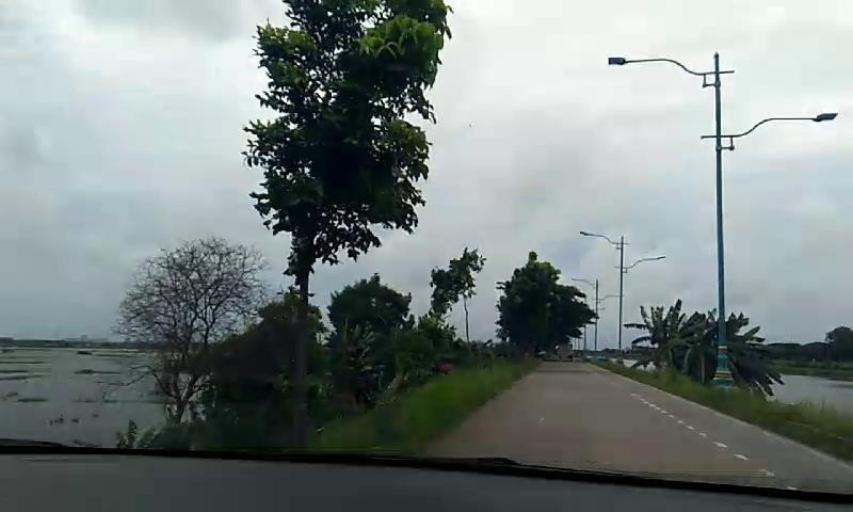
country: ID
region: West Java
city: Bekasi
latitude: -6.1294
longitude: 106.9691
